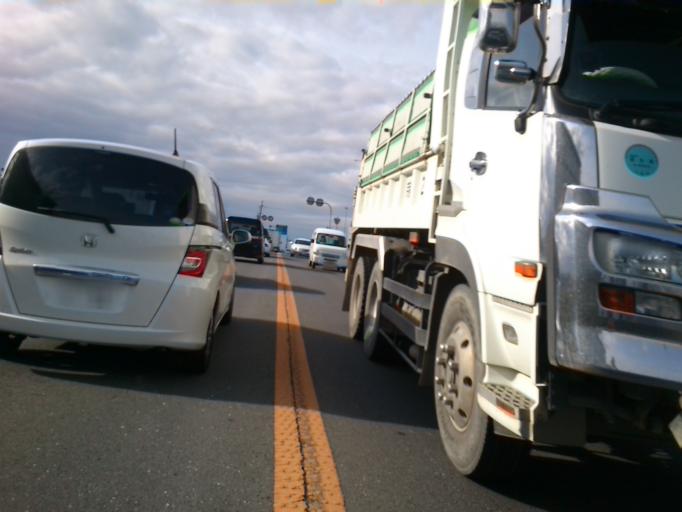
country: JP
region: Kyoto
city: Tanabe
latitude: 34.7682
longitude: 135.8075
